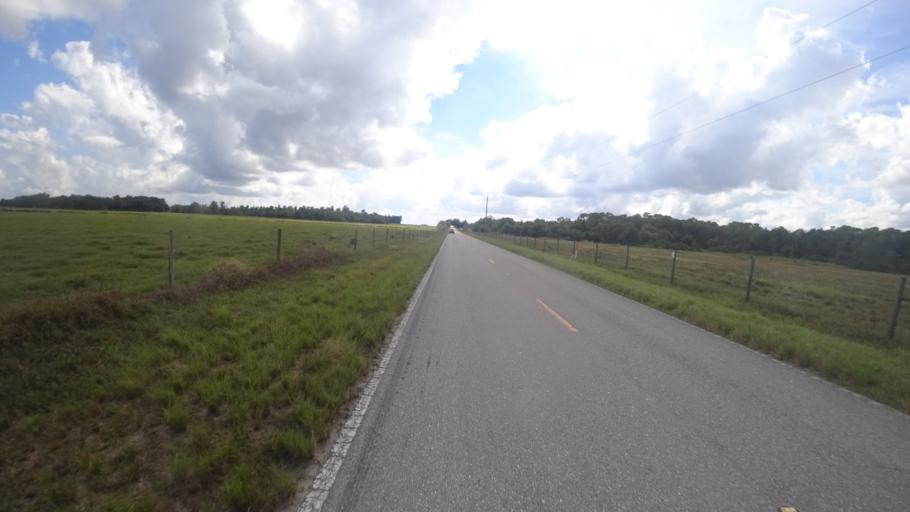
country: US
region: Florida
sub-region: Hillsborough County
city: Wimauma
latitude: 27.6356
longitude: -82.2310
